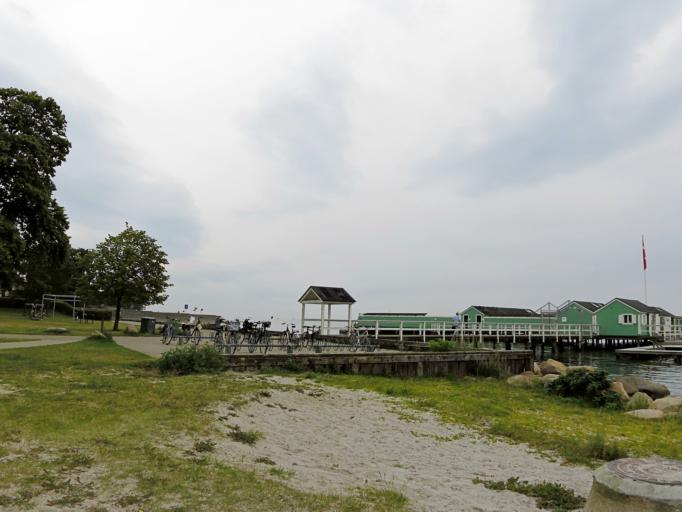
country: DK
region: Capital Region
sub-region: Gentofte Kommune
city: Charlottenlund
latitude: 55.7492
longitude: 12.5901
